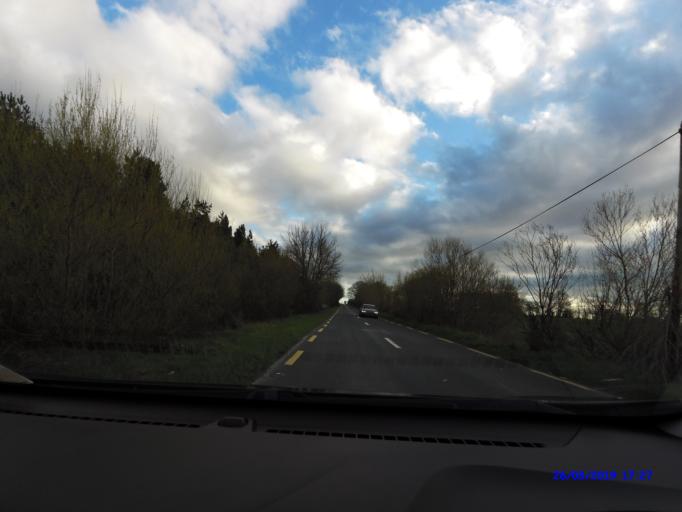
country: IE
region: Connaught
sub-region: Maigh Eo
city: Ballyhaunis
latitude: 53.7130
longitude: -8.7623
